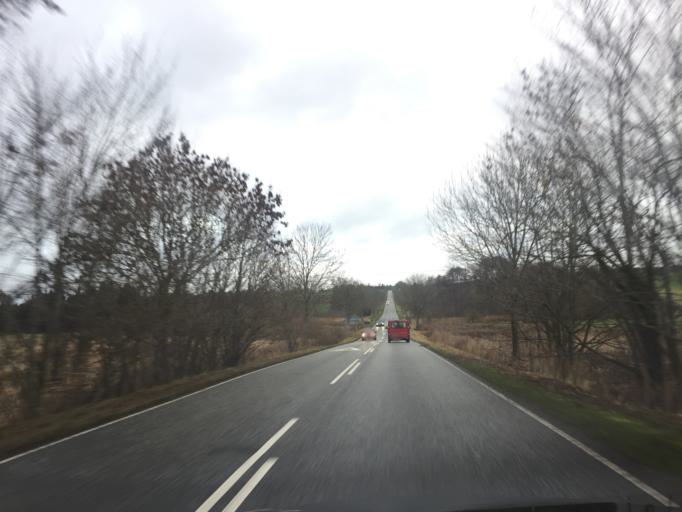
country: DK
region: Zealand
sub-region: Holbaek Kommune
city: Tollose
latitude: 55.6342
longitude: 11.7966
